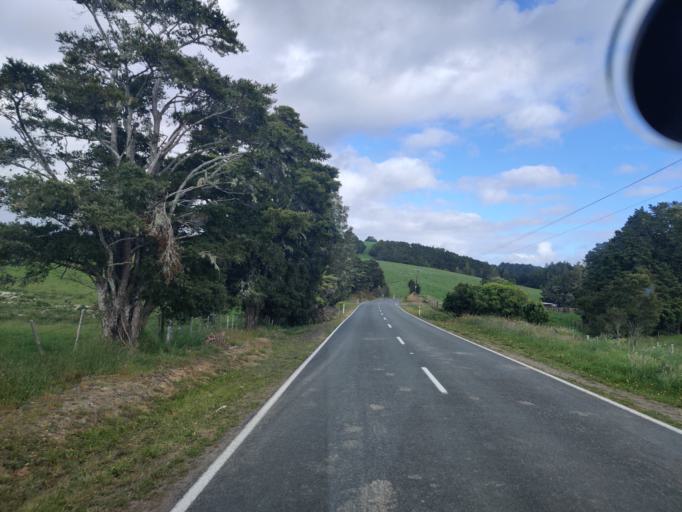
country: NZ
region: Northland
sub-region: Whangarei
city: Ngunguru
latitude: -35.5793
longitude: 174.4192
